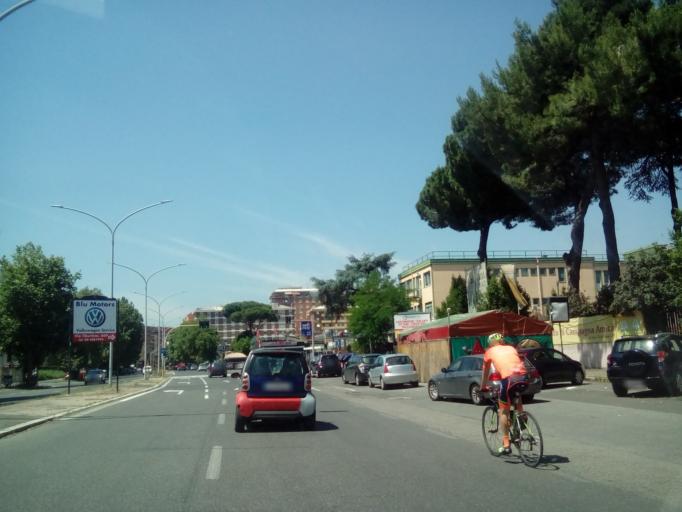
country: IT
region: Latium
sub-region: Citta metropolitana di Roma Capitale
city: Rome
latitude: 41.9112
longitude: 12.5503
